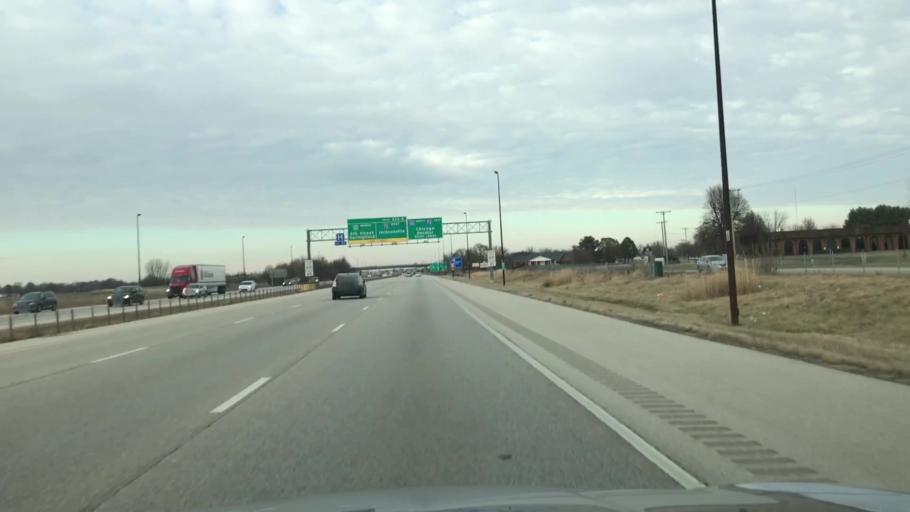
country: US
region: Illinois
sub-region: Sangamon County
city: Southern View
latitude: 39.7233
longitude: -89.6438
